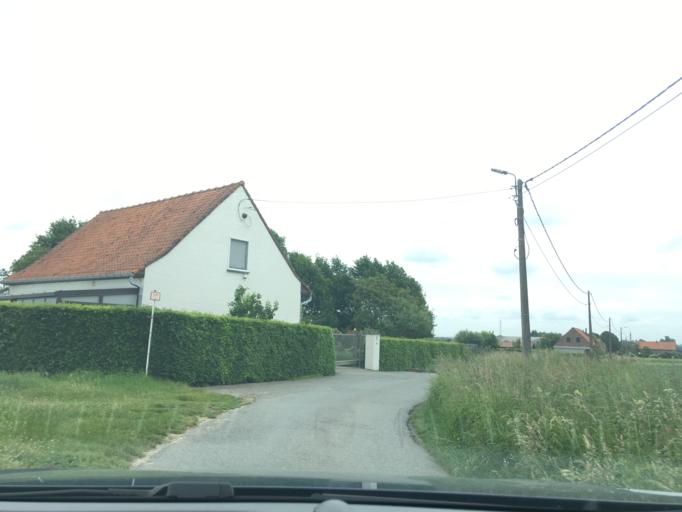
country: BE
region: Flanders
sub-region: Provincie West-Vlaanderen
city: Moorslede
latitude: 50.8371
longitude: 3.0703
